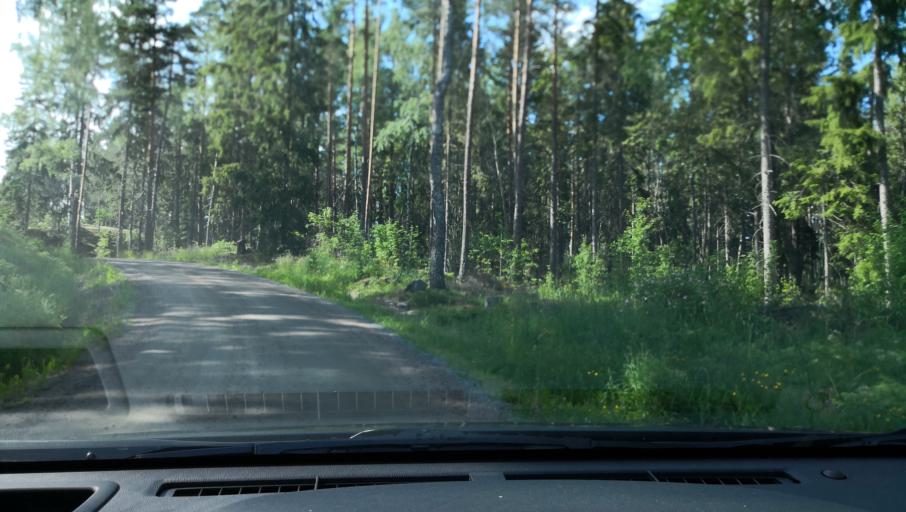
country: SE
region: Uppsala
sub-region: Enkopings Kommun
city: Orsundsbro
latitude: 59.8384
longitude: 17.2109
